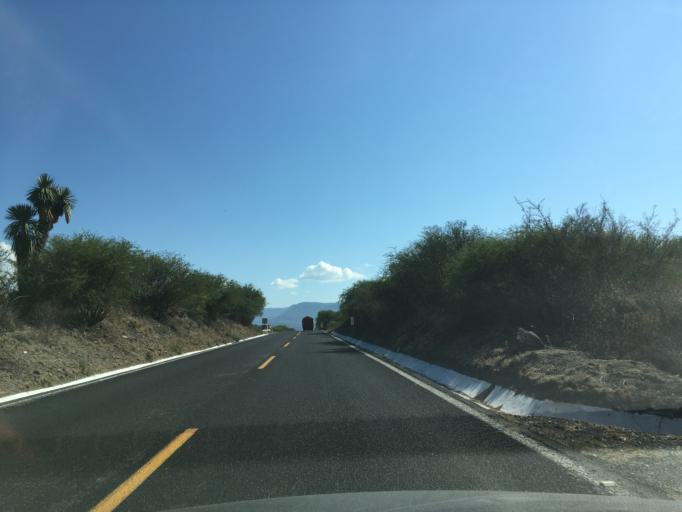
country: MX
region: Hidalgo
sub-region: San Agustin Metzquititlan
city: Mezquititlan
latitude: 20.4955
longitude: -98.6692
